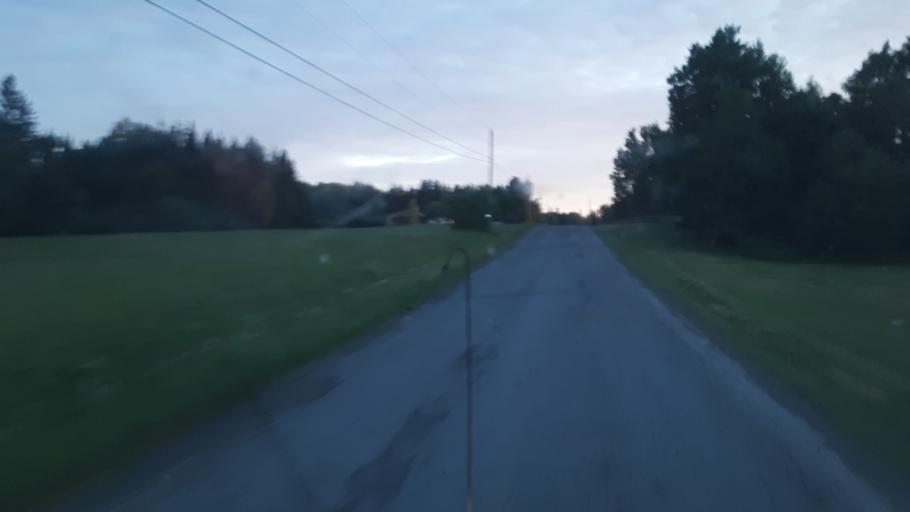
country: US
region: Maine
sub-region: Aroostook County
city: Caribou
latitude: 46.8681
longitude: -68.0921
